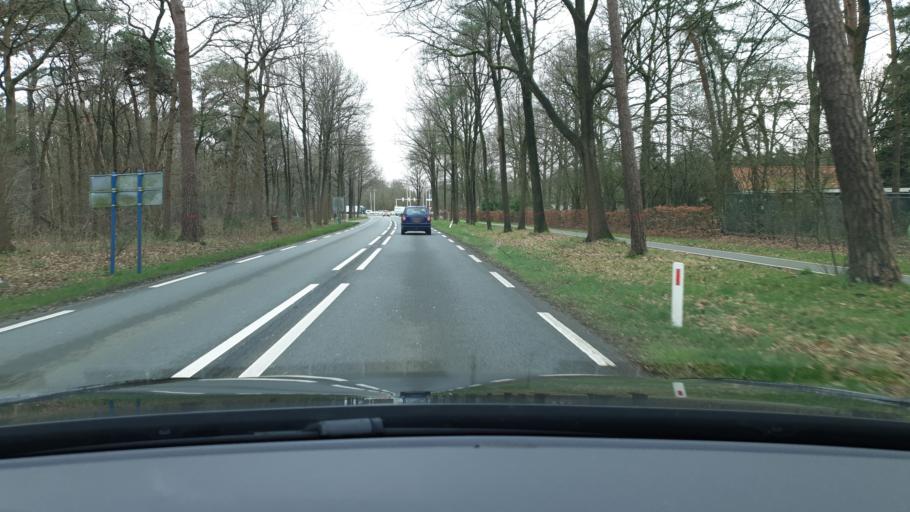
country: NL
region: North Brabant
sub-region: Gemeente Dongen
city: Dongen
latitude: 51.5824
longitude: 4.9074
